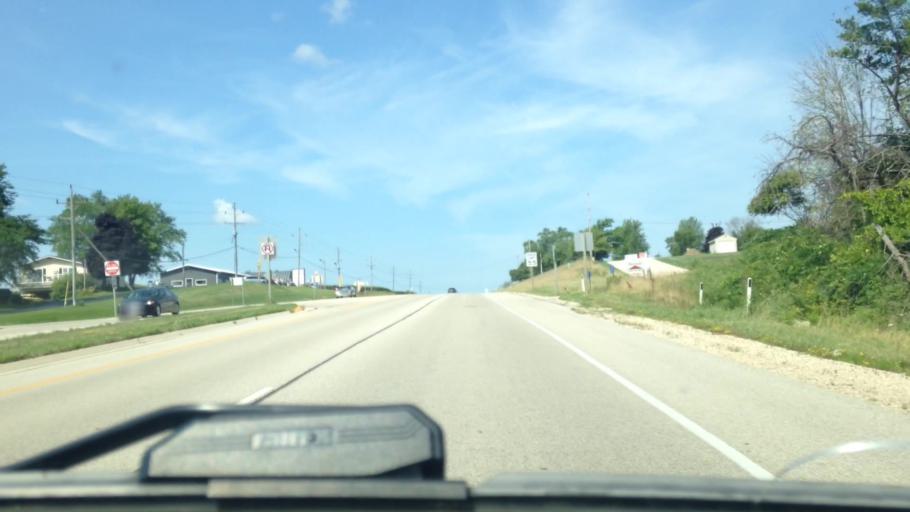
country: US
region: Wisconsin
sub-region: Washington County
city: West Bend
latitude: 43.4278
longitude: -88.2633
